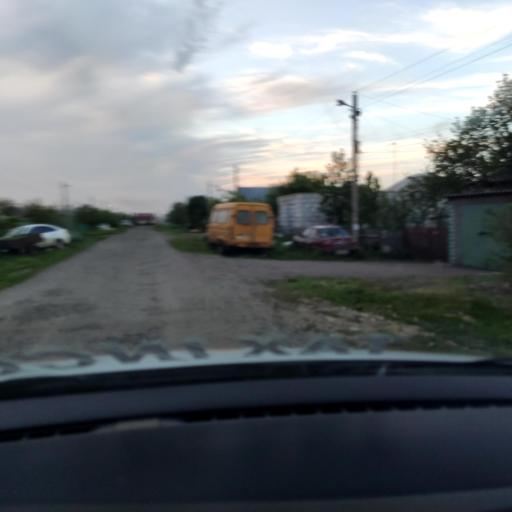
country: RU
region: Voronezj
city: Maslovka
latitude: 51.4540
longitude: 39.2377
